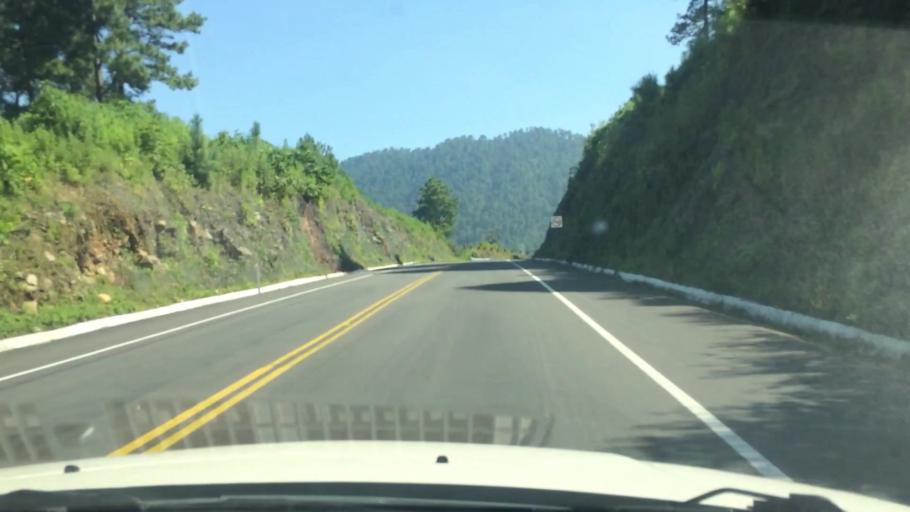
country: MX
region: Mexico
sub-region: Amanalco
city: Polvillos (San Bartolo Quinta Seccion)
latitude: 19.2264
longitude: -100.0836
